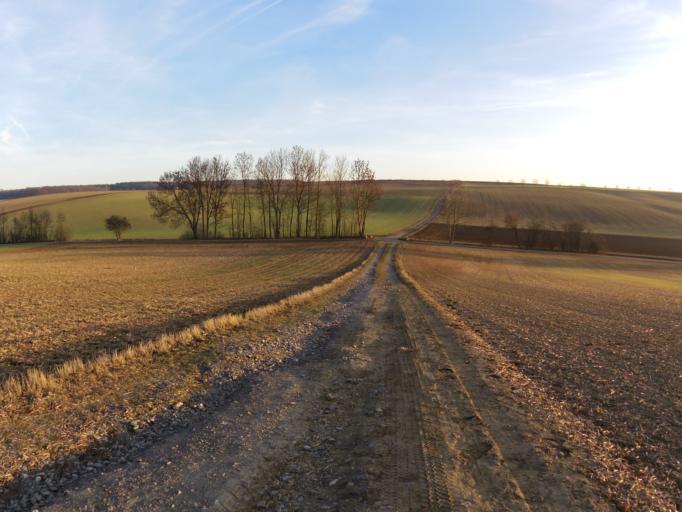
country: DE
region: Bavaria
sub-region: Regierungsbezirk Unterfranken
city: Estenfeld
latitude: 49.8222
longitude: 10.0218
